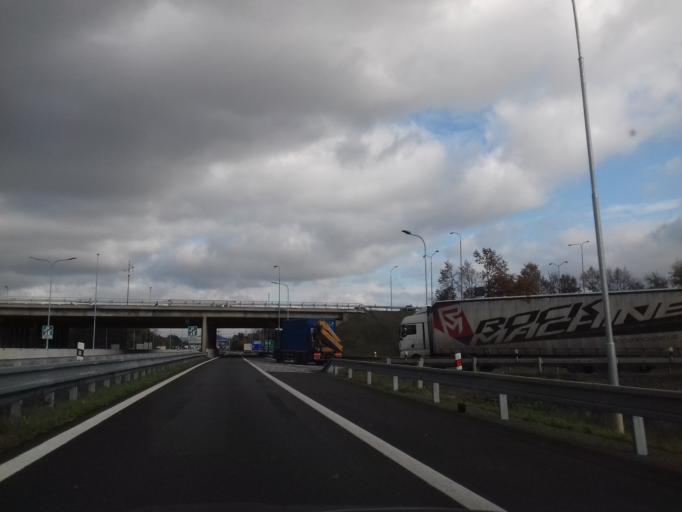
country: CZ
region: South Moravian
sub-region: Mesto Brno
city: Brno
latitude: 49.1584
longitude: 16.6311
